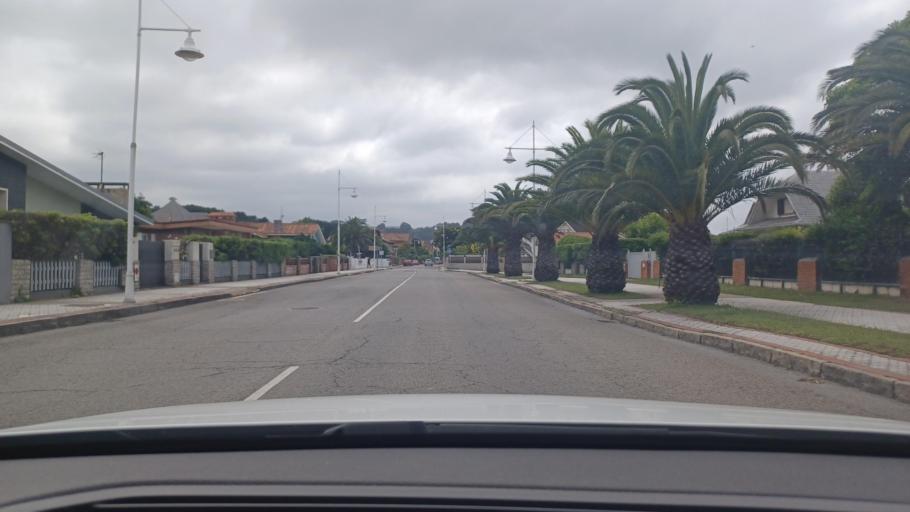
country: ES
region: Asturias
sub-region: Province of Asturias
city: Aviles
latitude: 43.5779
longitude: -5.9533
